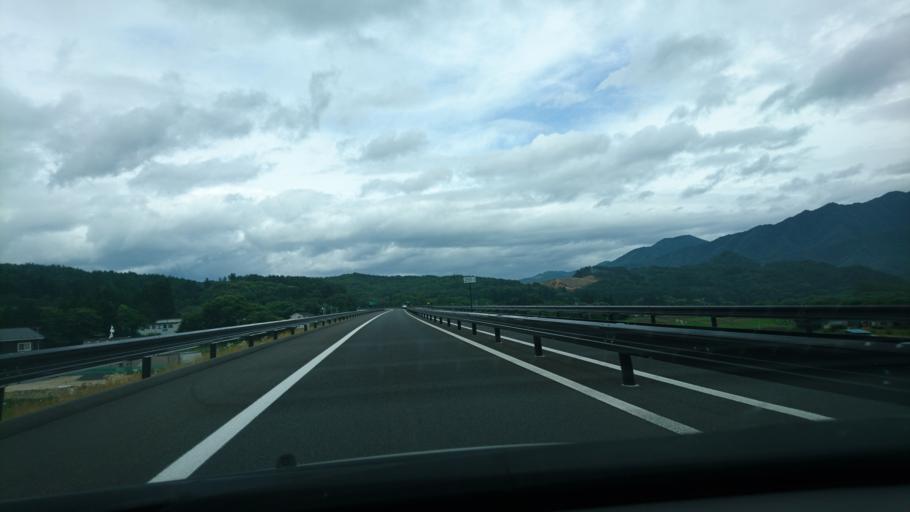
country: JP
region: Iwate
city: Yamada
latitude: 39.5413
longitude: 141.9211
